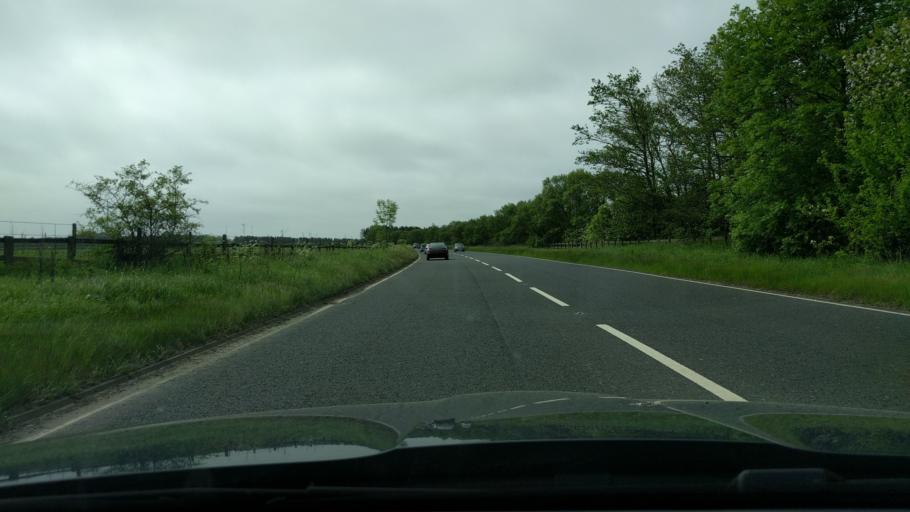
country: GB
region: England
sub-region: Northumberland
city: East Chevington
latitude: 55.2678
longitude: -1.6055
